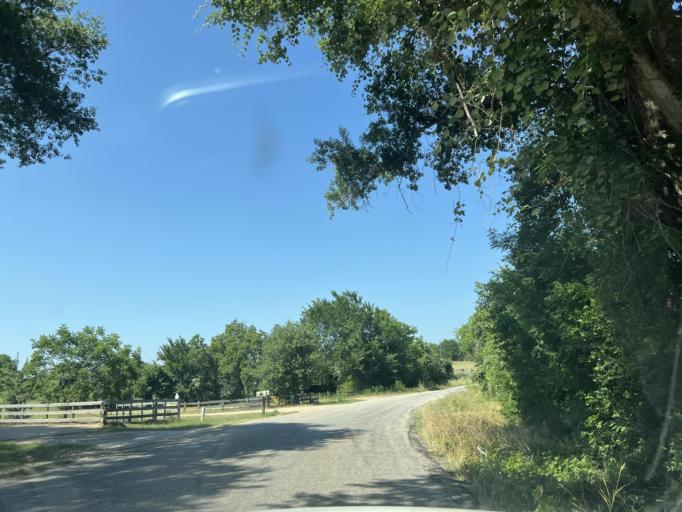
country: US
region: Texas
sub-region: Washington County
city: Brenham
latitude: 30.1751
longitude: -96.3545
